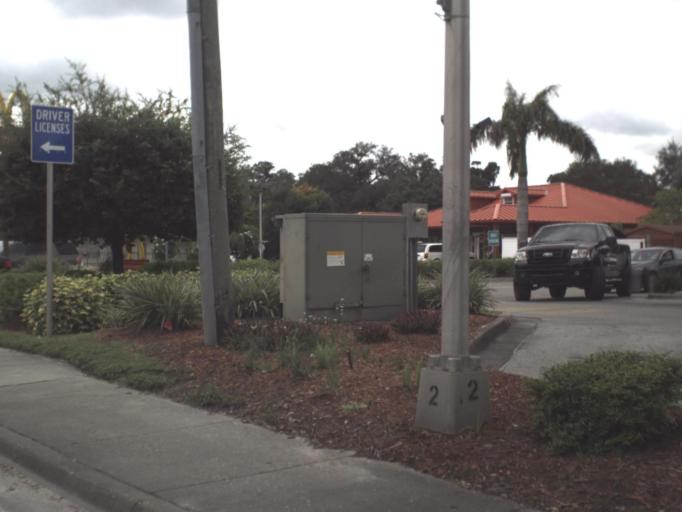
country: US
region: Florida
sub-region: Hendry County
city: LaBelle
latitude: 26.7613
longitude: -81.4385
